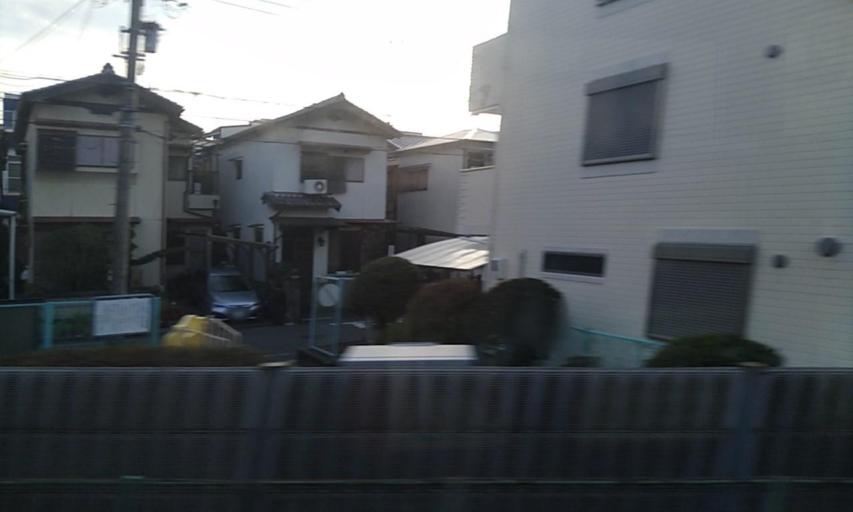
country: JP
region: Osaka
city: Ibaraki
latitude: 34.7949
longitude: 135.5599
